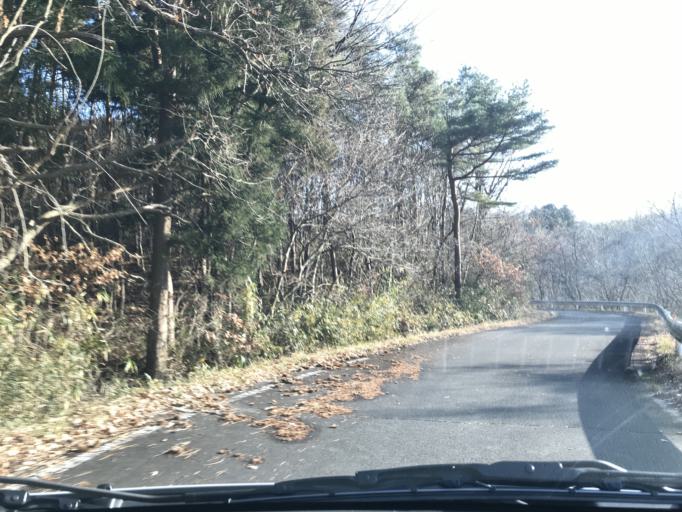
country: JP
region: Miyagi
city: Wakuya
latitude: 38.6843
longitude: 141.1288
